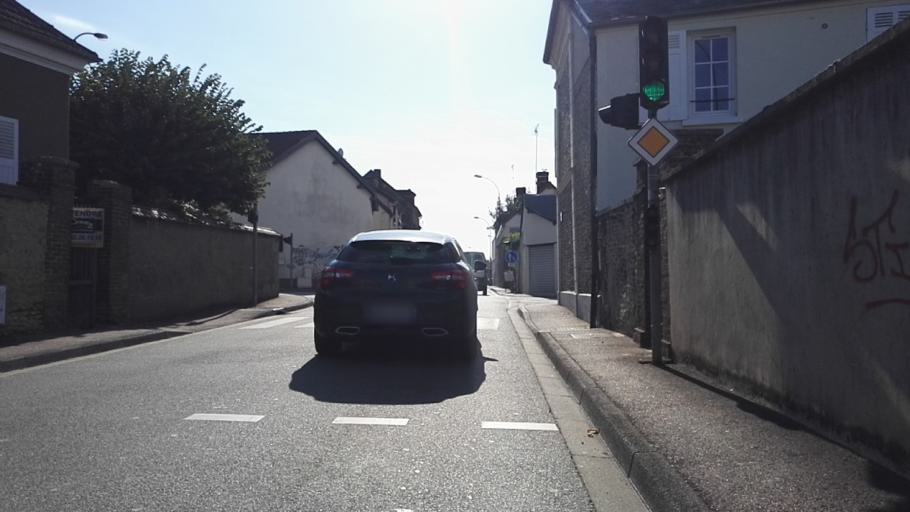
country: FR
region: Haute-Normandie
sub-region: Departement de l'Eure
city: Pacy-sur-Eure
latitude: 49.0163
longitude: 1.3833
